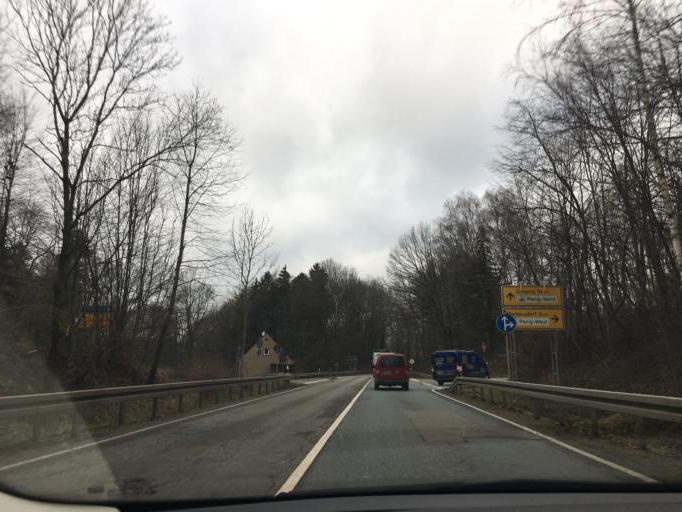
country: DE
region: Saxony
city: Penig
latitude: 50.9326
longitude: 12.6869
